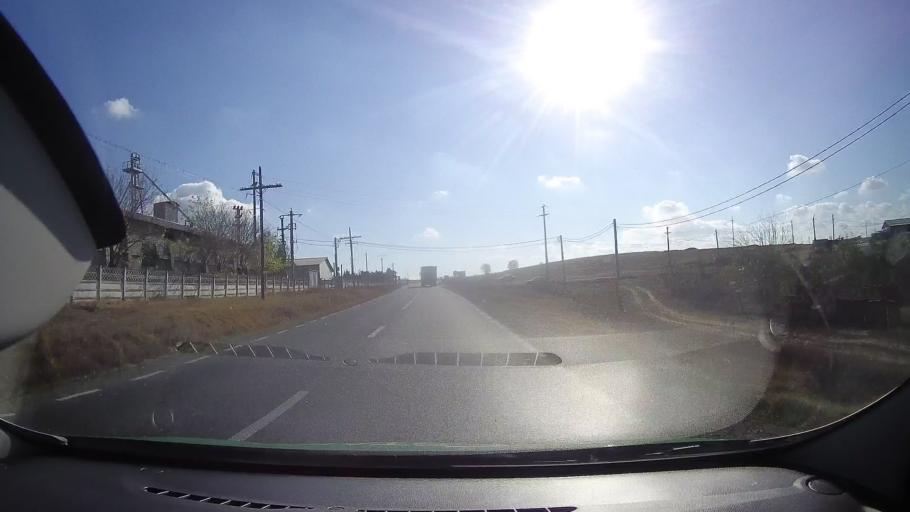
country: RO
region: Tulcea
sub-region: Comuna Baia
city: Baia
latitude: 44.7176
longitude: 28.6809
